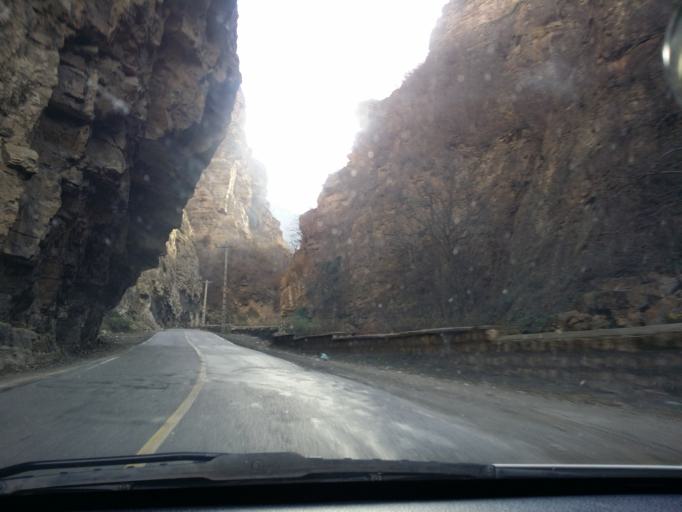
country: IR
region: Mazandaran
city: Chalus
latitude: 36.2710
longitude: 51.2457
